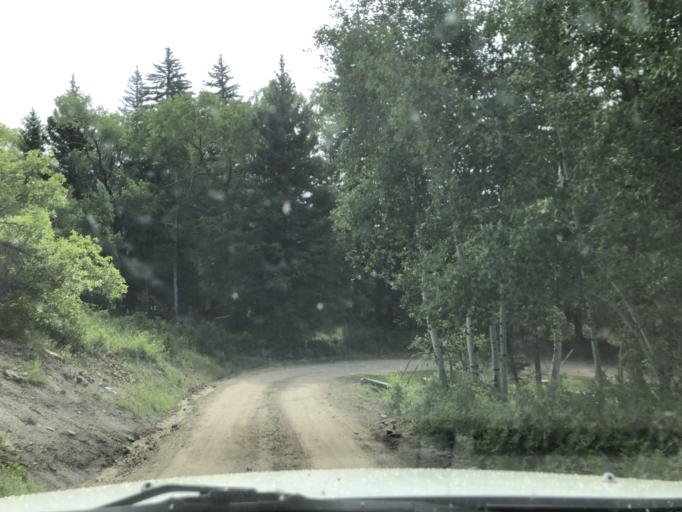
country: US
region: Colorado
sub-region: Delta County
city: Paonia
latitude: 39.0269
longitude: -107.3435
